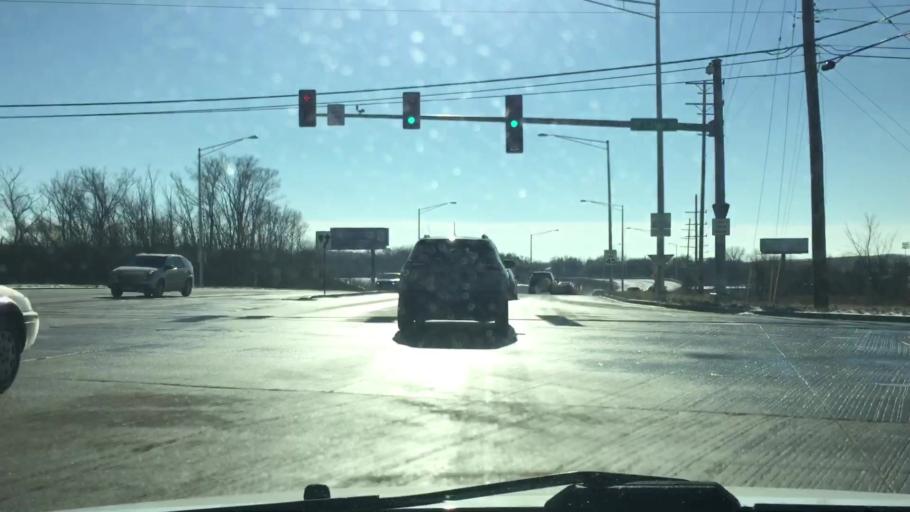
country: US
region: Illinois
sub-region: Kane County
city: Geneva
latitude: 41.8861
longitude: -88.2773
